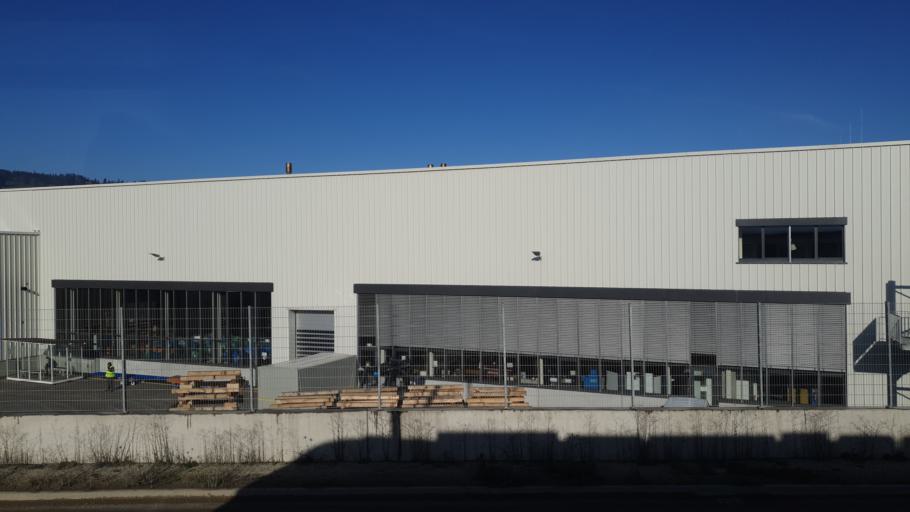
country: CH
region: Fribourg
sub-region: Gruyere District
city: Bulle
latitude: 46.6214
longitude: 7.0385
